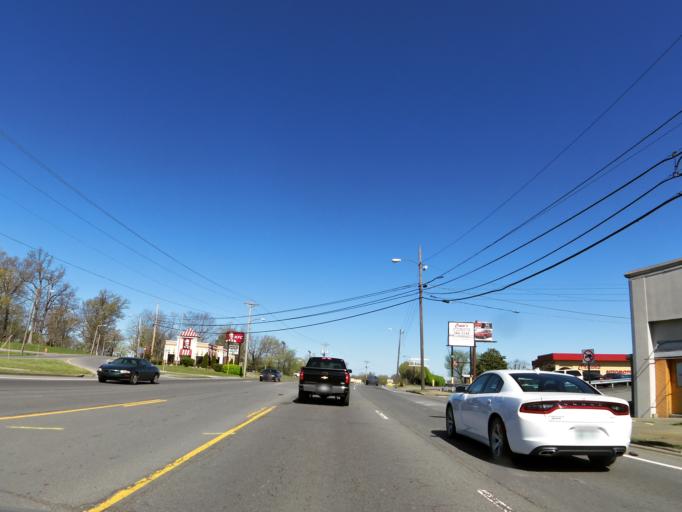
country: US
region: Tennessee
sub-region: Robertson County
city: Springfield
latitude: 36.4954
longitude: -86.8800
